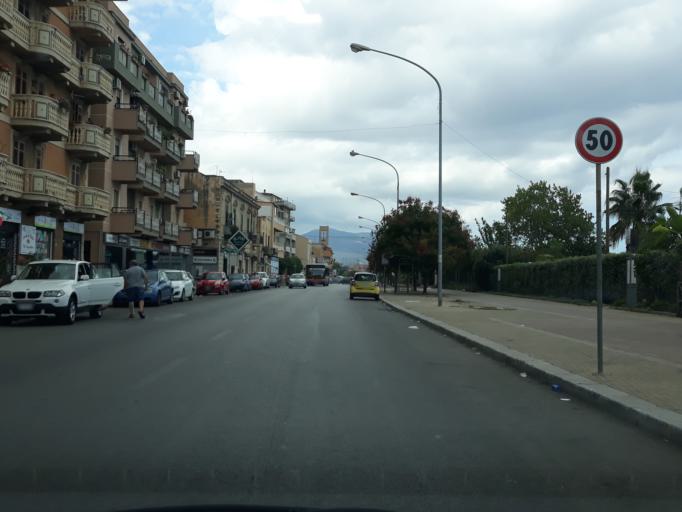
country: IT
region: Sicily
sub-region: Palermo
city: Ciaculli
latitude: 38.1041
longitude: 13.3915
